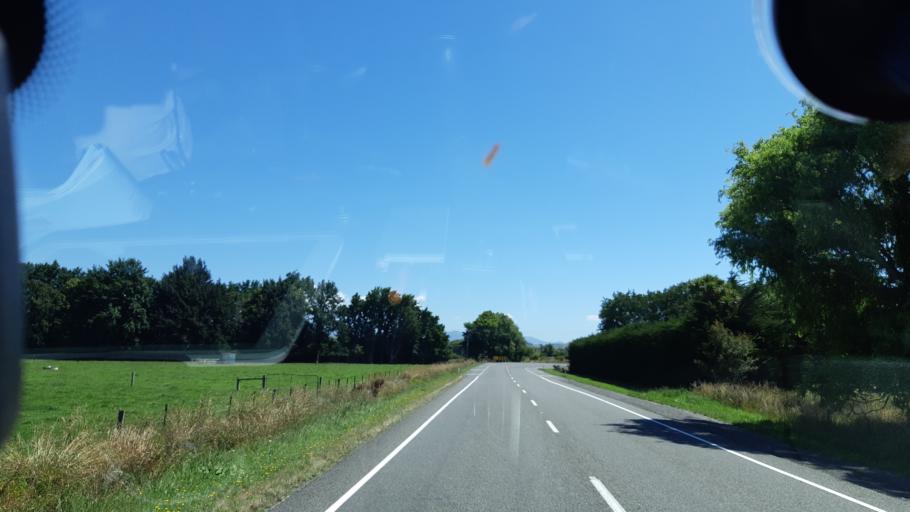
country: NZ
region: Canterbury
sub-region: Kaikoura District
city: Kaikoura
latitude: -42.7413
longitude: 173.2667
